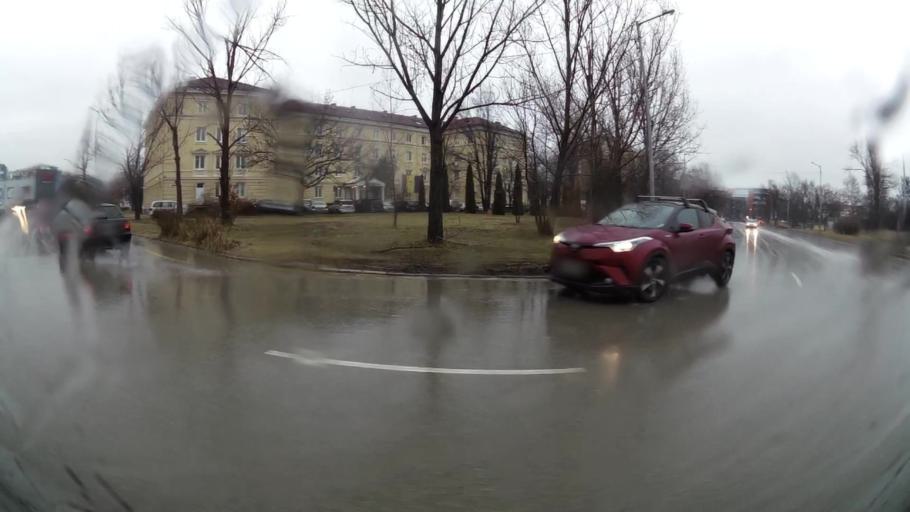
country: BG
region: Sofia-Capital
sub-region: Stolichna Obshtina
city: Sofia
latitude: 42.6545
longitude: 23.3493
